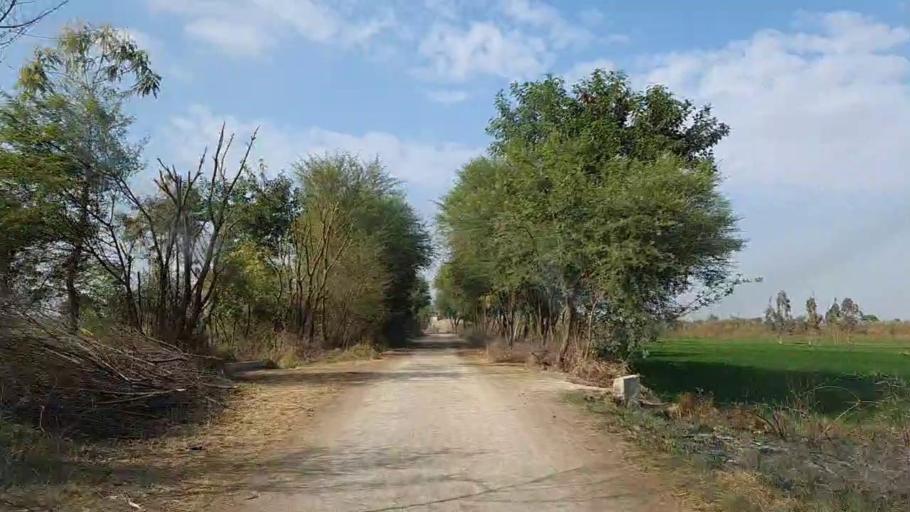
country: PK
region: Sindh
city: Sanghar
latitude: 26.2499
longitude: 69.0134
